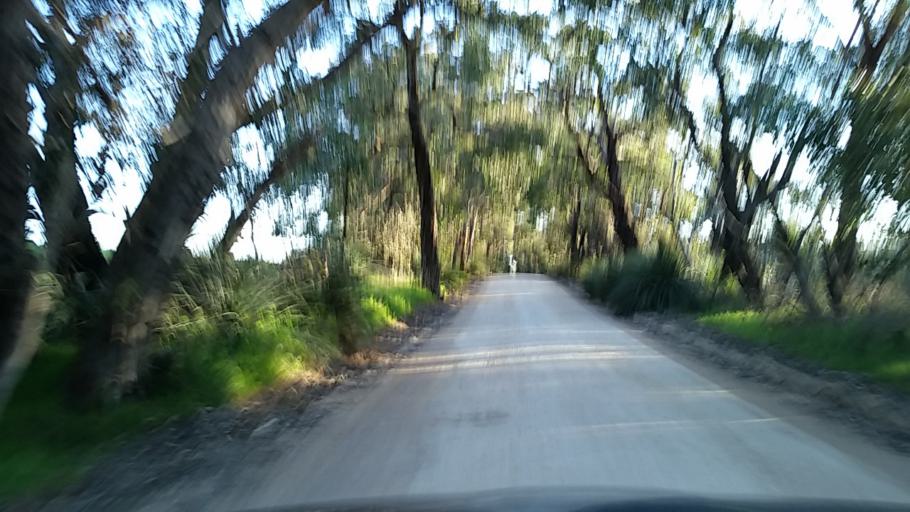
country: AU
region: South Australia
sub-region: Alexandrina
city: Mount Compass
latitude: -35.3109
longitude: 138.6716
